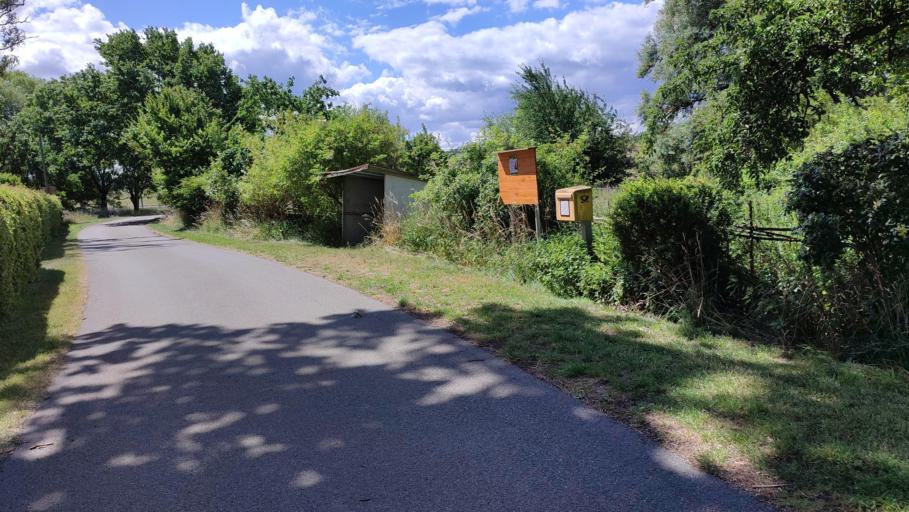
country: DE
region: Lower Saxony
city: Hitzacker
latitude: 53.1965
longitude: 10.9831
